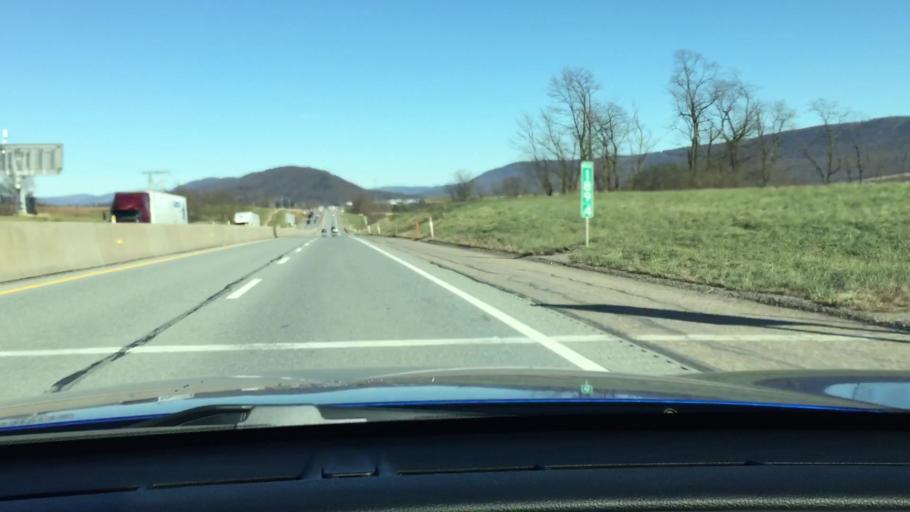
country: US
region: Pennsylvania
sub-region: Franklin County
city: Doylestown
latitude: 40.1039
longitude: -77.8035
